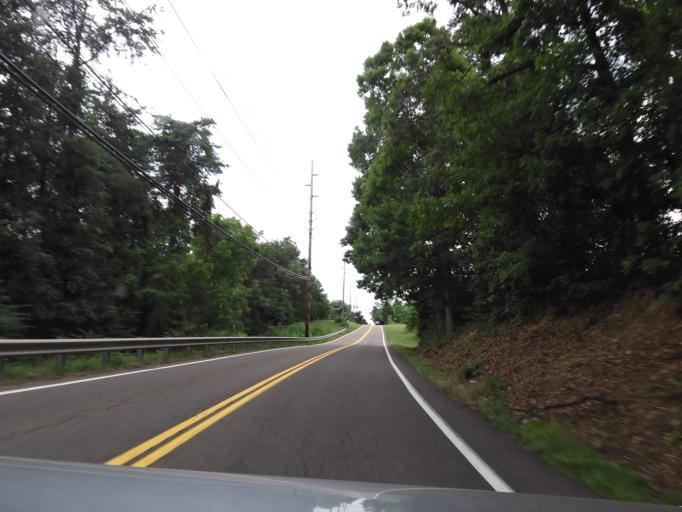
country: US
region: Tennessee
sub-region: Knox County
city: Farragut
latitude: 35.8544
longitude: -84.1104
